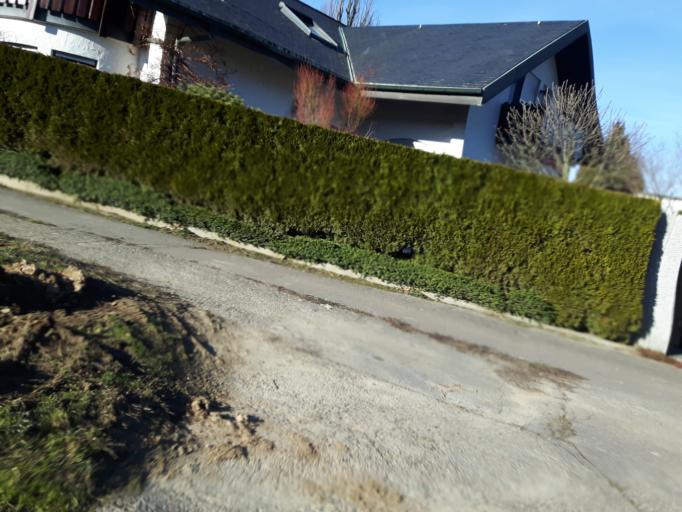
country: DE
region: Baden-Wuerttemberg
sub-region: Regierungsbezirk Stuttgart
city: Leingarten
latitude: 49.1396
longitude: 9.1146
